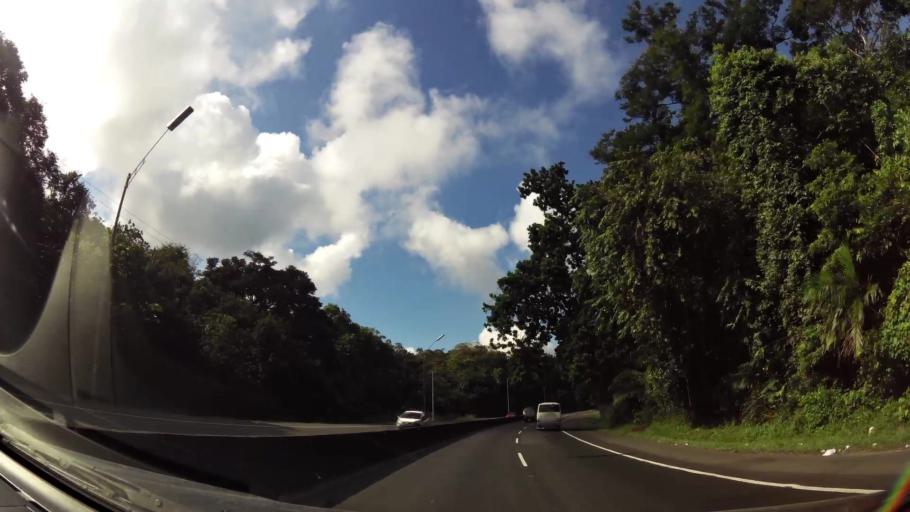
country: PA
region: Panama
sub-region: Distrito Arraijan
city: Arraijan
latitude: 8.9551
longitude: -79.6224
